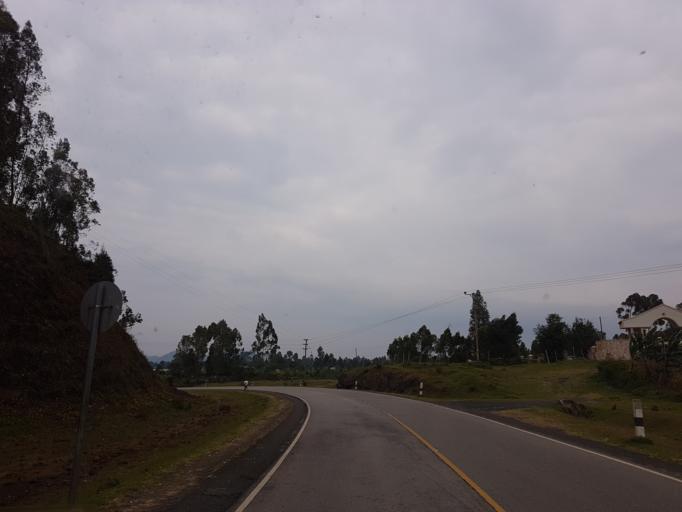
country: UG
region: Western Region
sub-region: Kisoro District
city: Kisoro
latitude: -1.3315
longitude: 29.7345
